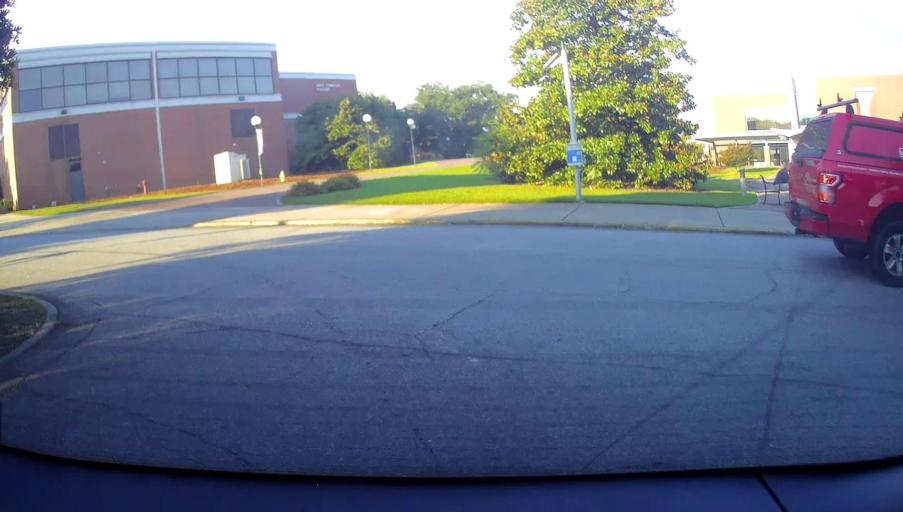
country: US
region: Georgia
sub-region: Bibb County
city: West Point
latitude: 32.8090
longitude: -83.7331
